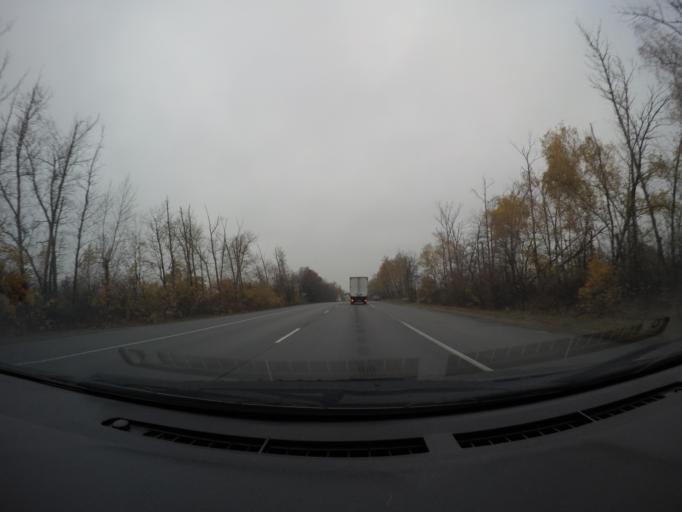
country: RU
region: Moskovskaya
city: Zhitnevo
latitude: 55.3573
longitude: 37.9213
